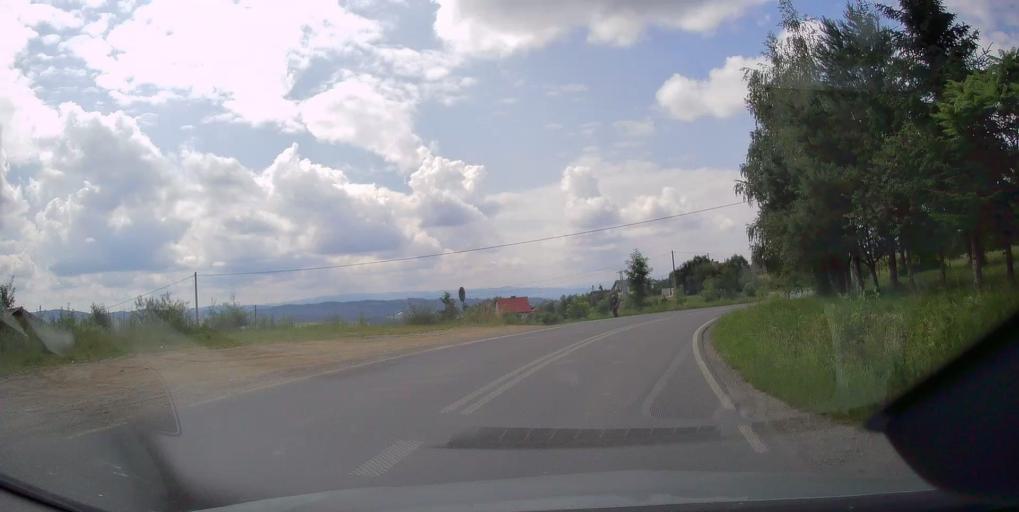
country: PL
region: Lesser Poland Voivodeship
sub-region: Powiat nowosadecki
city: Korzenna
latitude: 49.6905
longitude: 20.7771
